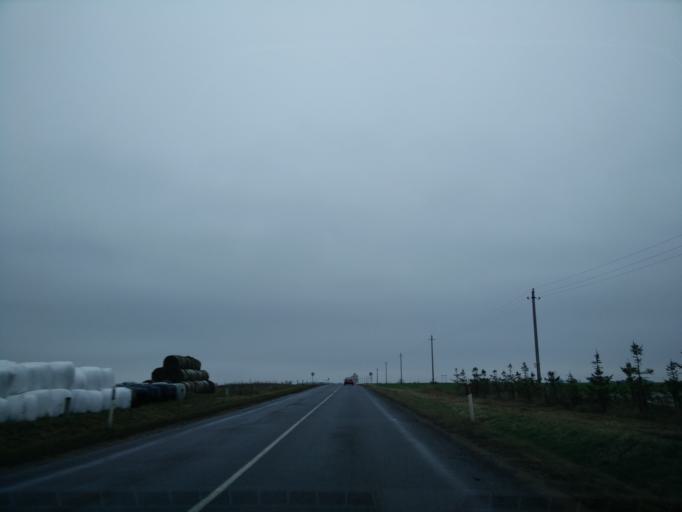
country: LT
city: Ariogala
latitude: 55.3065
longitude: 23.4324
